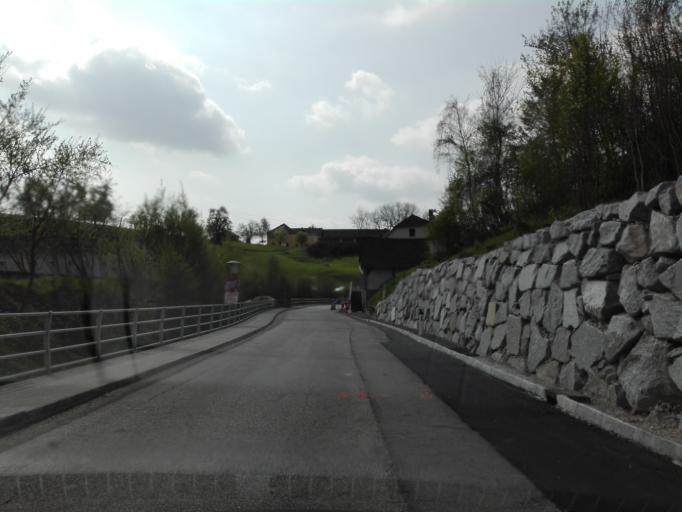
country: AT
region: Upper Austria
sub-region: Politischer Bezirk Perg
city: Perg
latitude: 48.2337
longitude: 14.7055
